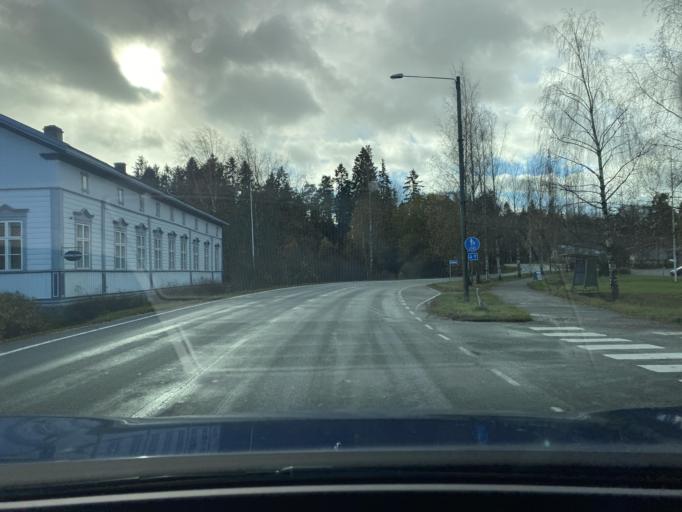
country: FI
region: Varsinais-Suomi
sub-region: Loimaa
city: Aura
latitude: 60.7181
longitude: 22.6025
